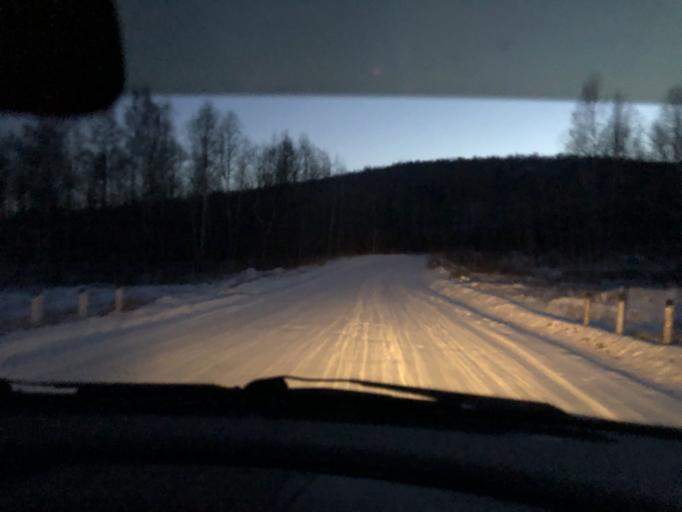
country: RU
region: Khabarovsk Krai
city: Amursk
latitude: 50.3117
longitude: 136.7888
